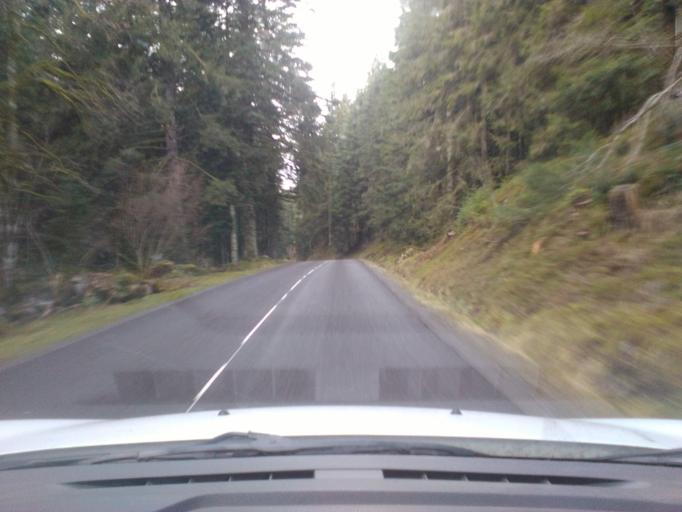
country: FR
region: Lorraine
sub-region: Departement des Vosges
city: Xonrupt-Longemer
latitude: 48.1067
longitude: 6.9719
